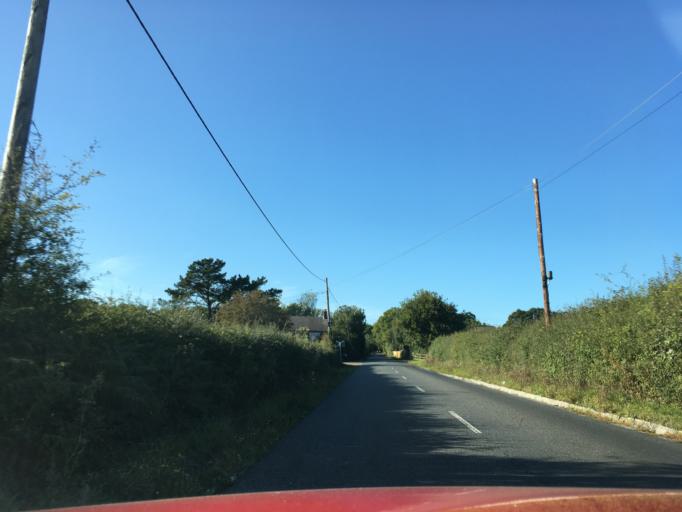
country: GB
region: England
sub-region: Hampshire
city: Swanmore
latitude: 50.9277
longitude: -1.1676
